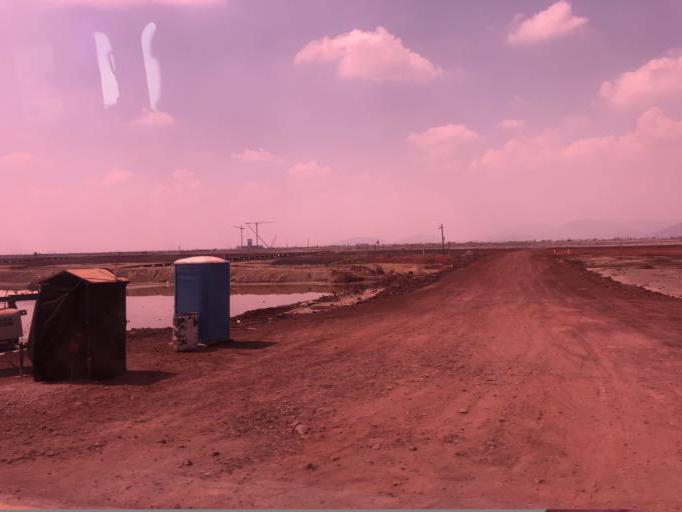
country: MX
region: Mexico
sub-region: Atenco
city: Colonia el Salado
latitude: 19.5273
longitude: -98.9856
